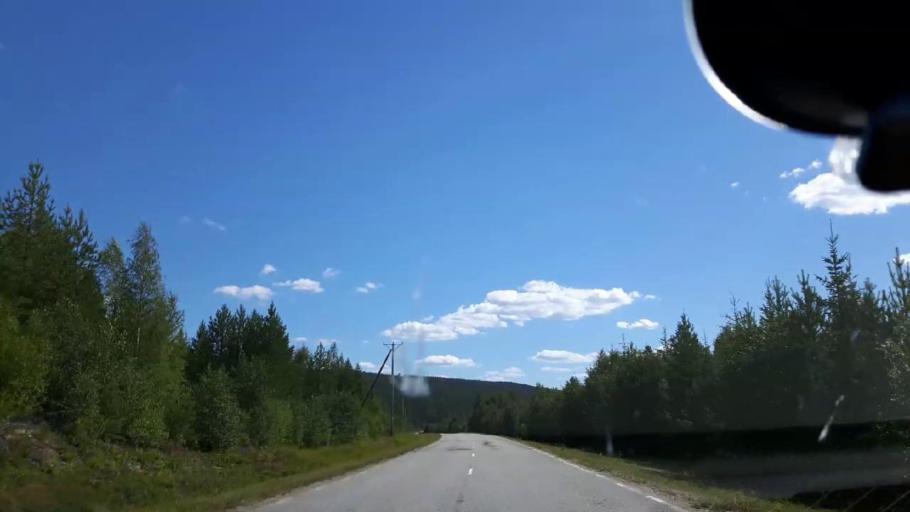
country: SE
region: Vaesternorrland
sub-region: Ange Kommun
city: Fransta
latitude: 62.7489
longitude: 16.3201
